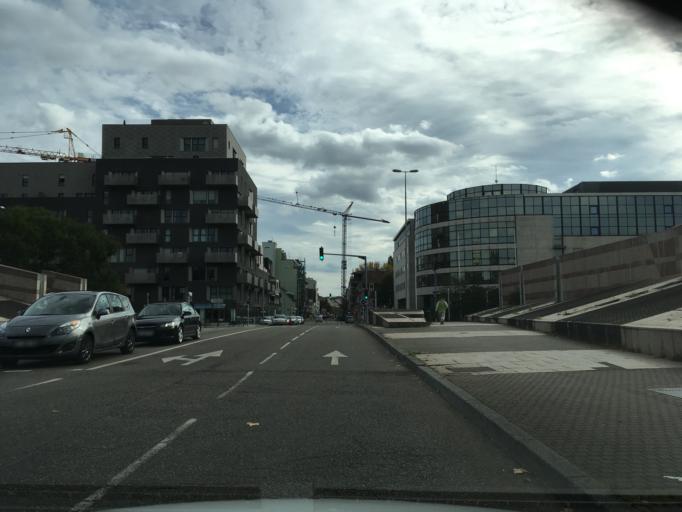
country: FR
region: Alsace
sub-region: Departement du Bas-Rhin
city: Strasbourg
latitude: 48.5724
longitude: 7.7503
